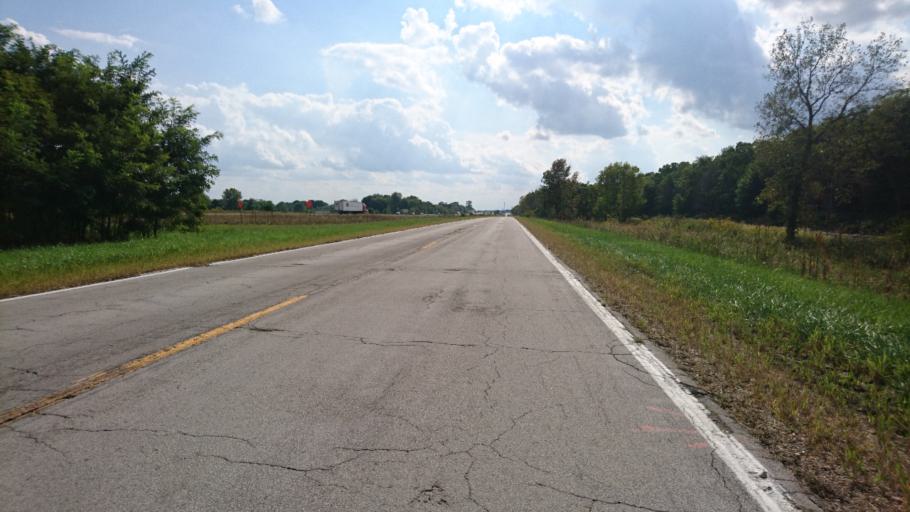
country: US
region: Illinois
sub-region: Logan County
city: Atlanta
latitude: 40.3454
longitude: -89.1333
